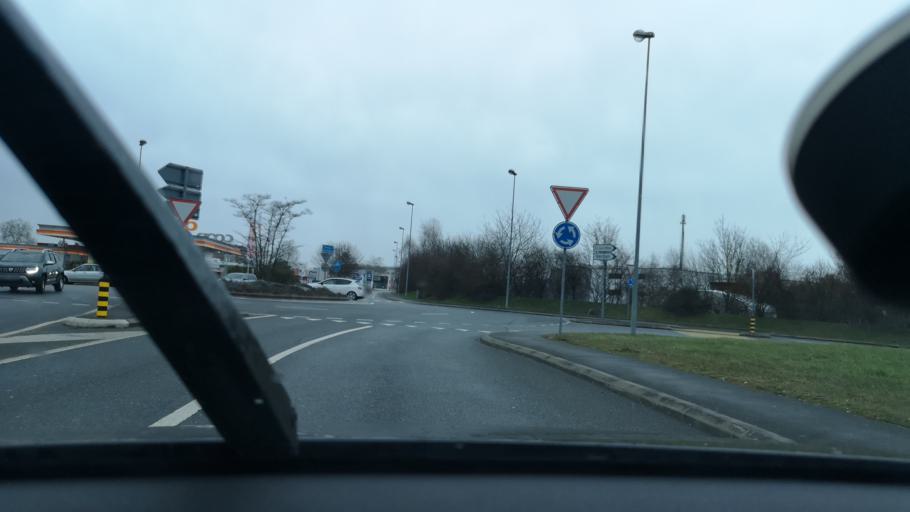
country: CH
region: Vaud
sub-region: Jura-Nord vaudois District
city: Montagny
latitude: 46.7891
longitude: 6.6244
